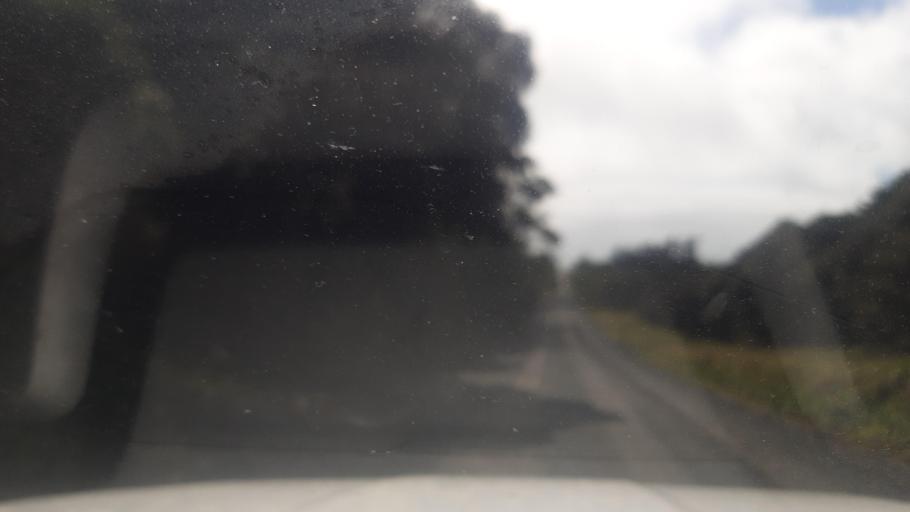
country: NZ
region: Northland
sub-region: Far North District
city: Kaitaia
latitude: -34.7424
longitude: 173.1101
